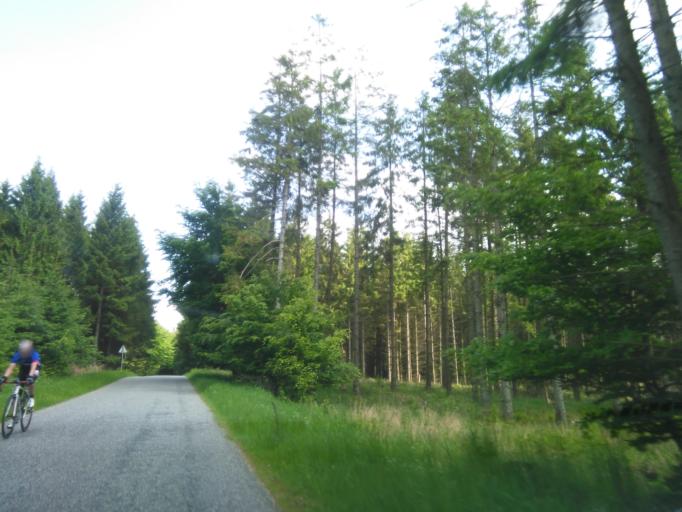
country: DK
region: Central Jutland
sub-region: Skanderborg Kommune
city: Galten
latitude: 56.2253
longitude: 9.9276
